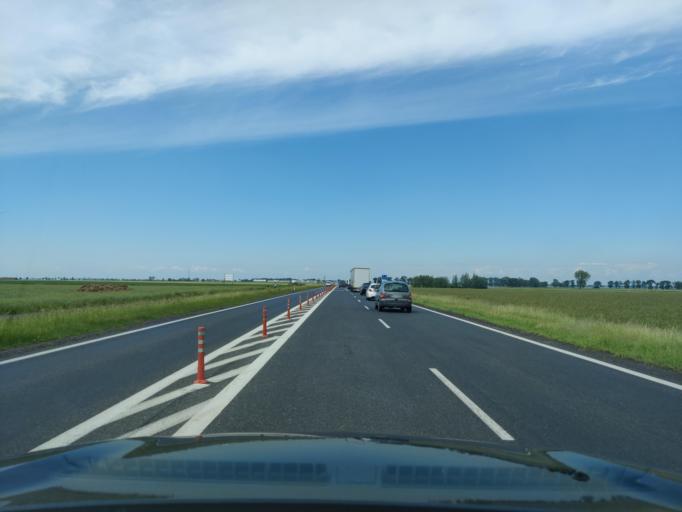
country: PL
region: Greater Poland Voivodeship
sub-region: Powiat grodziski
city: Granowo
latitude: 52.2214
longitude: 16.5712
